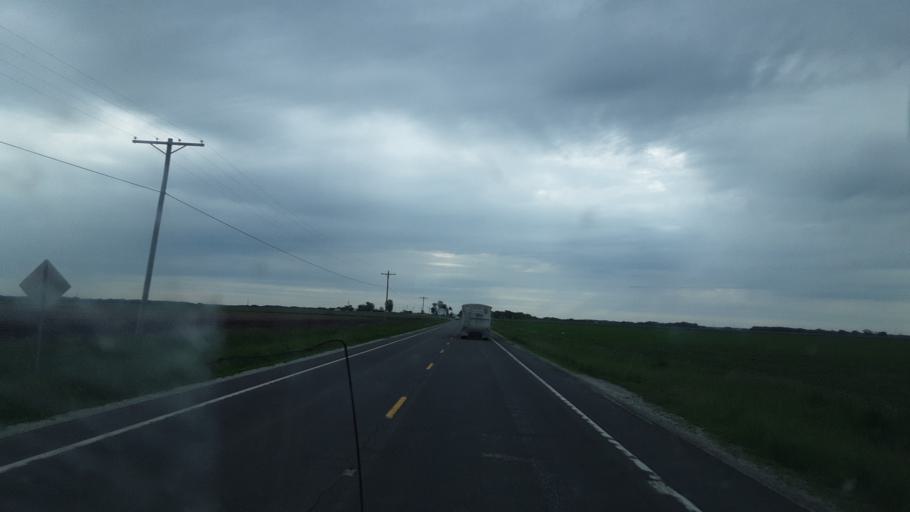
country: US
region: Illinois
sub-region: Fulton County
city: Lewistown
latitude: 40.3421
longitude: -90.2614
